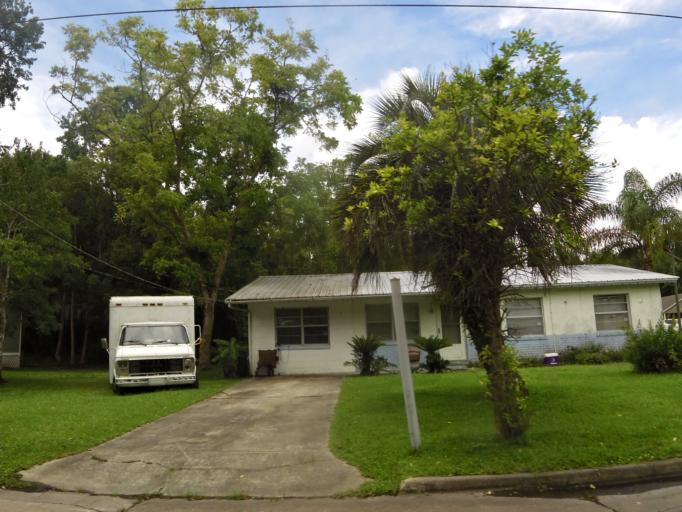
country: US
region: Florida
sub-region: Putnam County
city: East Palatka
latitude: 29.7170
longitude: -81.5055
